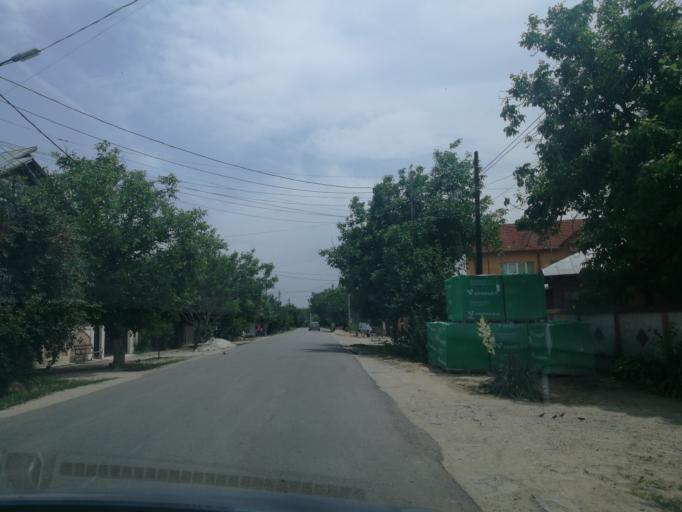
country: RO
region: Ilfov
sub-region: Comuna Vidra
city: Cretesti
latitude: 44.2725
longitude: 26.1442
